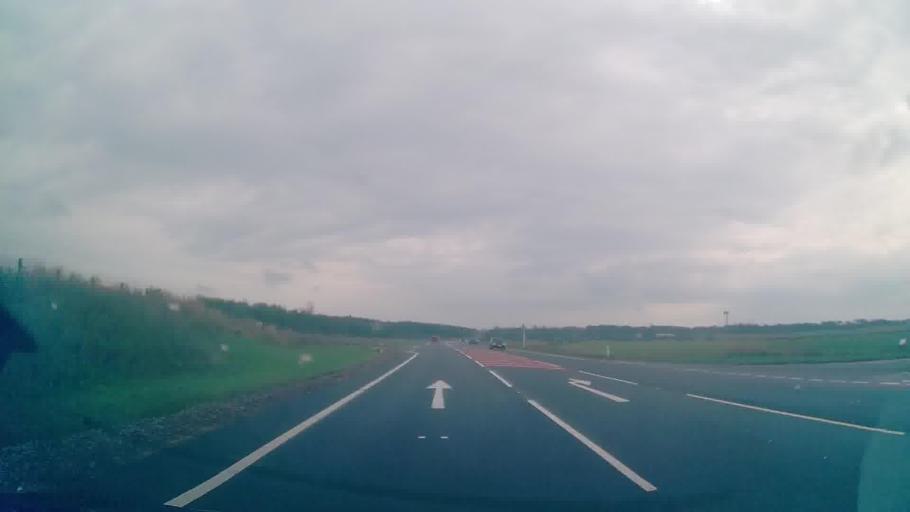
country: GB
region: Scotland
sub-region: Dumfries and Galloway
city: Lockerbie
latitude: 55.0196
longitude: -3.3669
